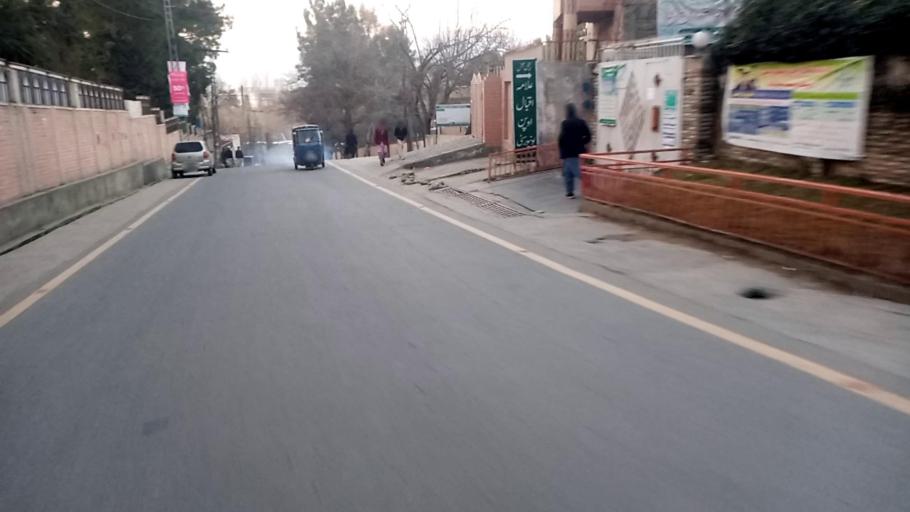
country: PK
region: Khyber Pakhtunkhwa
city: Saidu Sharif
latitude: 34.7569
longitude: 72.3606
